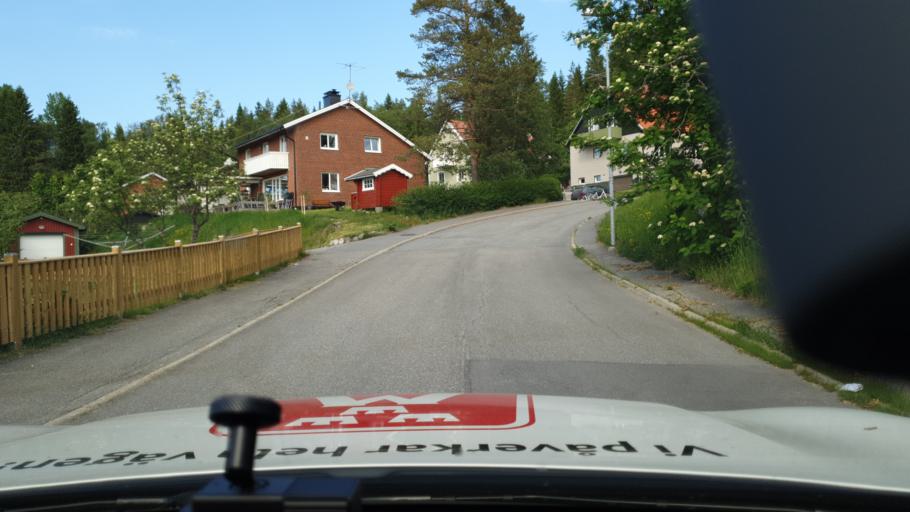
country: SE
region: Vaesterbotten
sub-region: Umea Kommun
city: Umea
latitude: 63.8396
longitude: 20.2865
